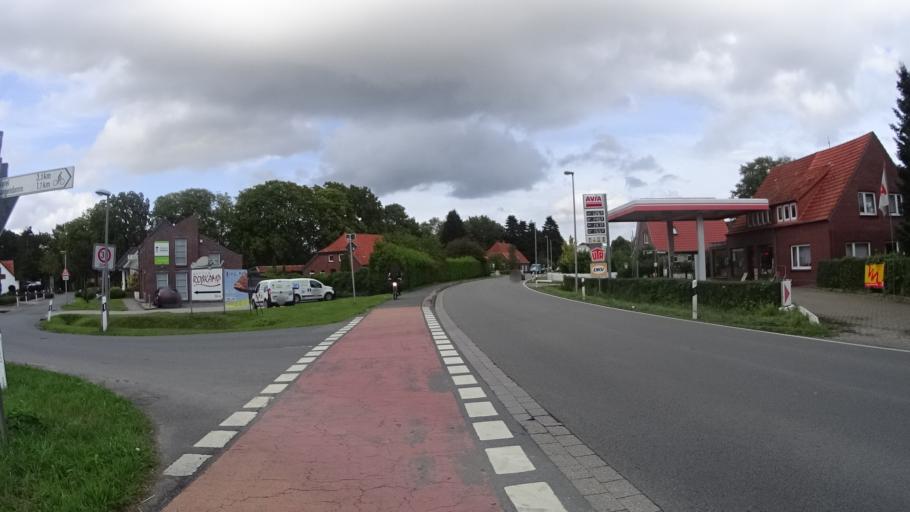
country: DE
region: Lower Saxony
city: Varel
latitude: 53.3933
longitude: 8.0910
